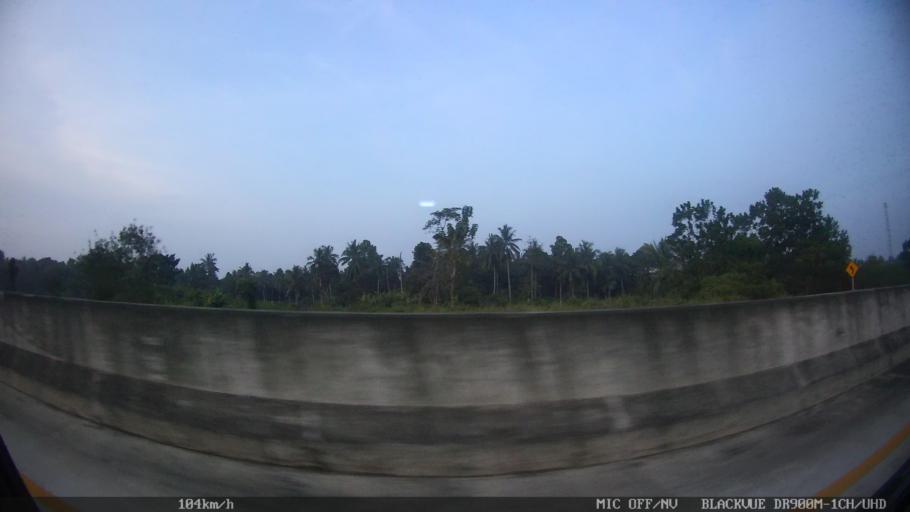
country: ID
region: Lampung
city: Pasuruan
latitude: -5.7089
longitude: 105.6448
